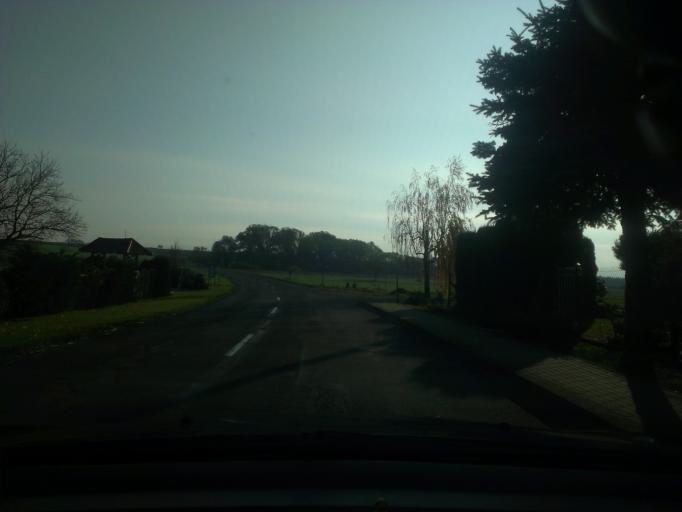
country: SK
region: Trnavsky
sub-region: Okres Trnava
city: Piestany
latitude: 48.5176
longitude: 17.9743
